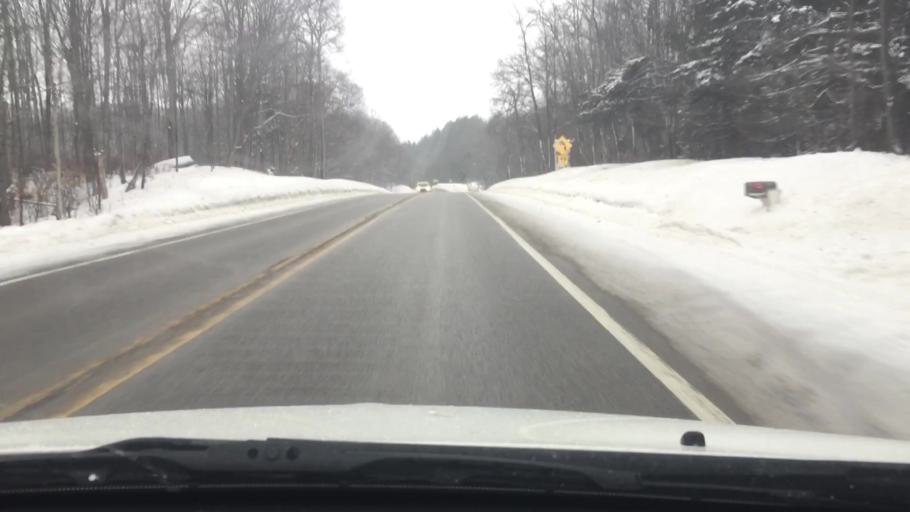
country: US
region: Michigan
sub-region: Otsego County
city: Gaylord
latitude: 45.0608
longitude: -84.7974
